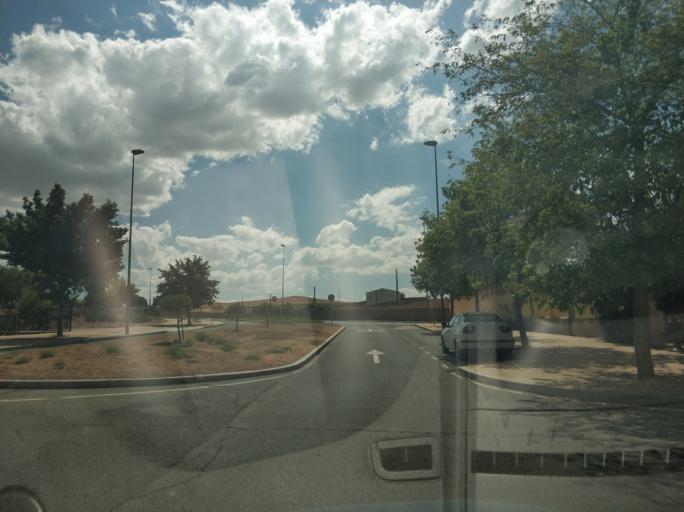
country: ES
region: Castille and Leon
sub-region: Provincia de Salamanca
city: Aldeatejada
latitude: 40.9513
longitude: -5.6935
